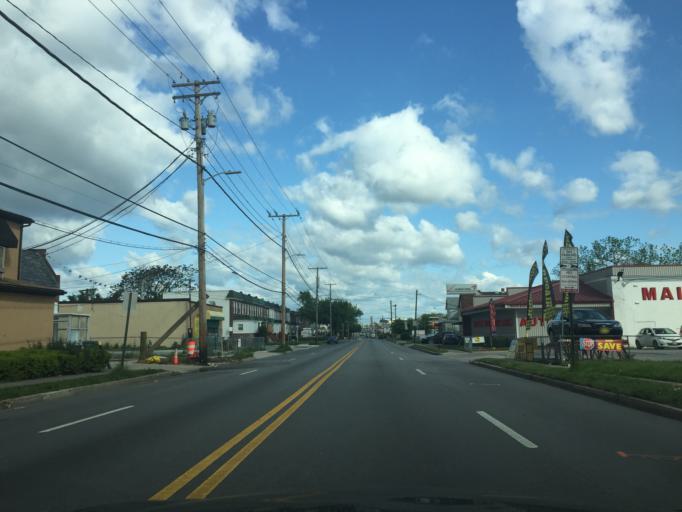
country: US
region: Maryland
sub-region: Baltimore County
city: Lochearn
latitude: 39.3451
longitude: -76.6866
